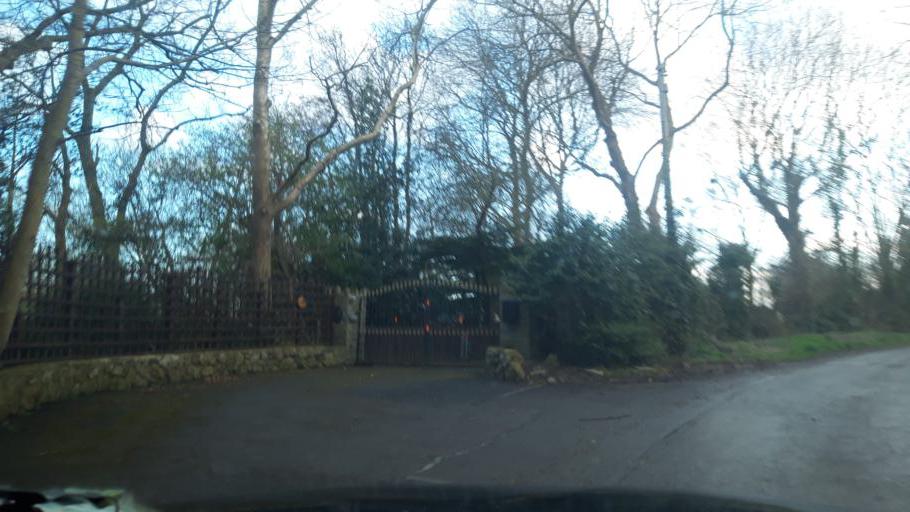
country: IE
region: Leinster
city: Donabate
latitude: 53.4768
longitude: -6.1636
